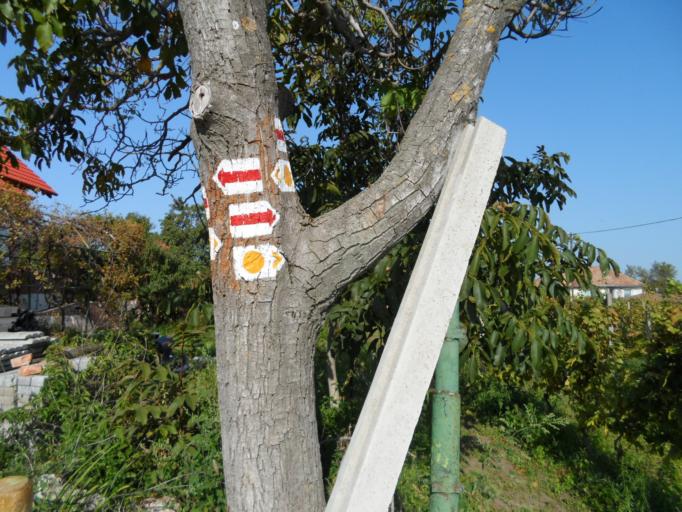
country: HU
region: Veszprem
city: Devecser
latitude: 47.1554
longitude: 17.3767
